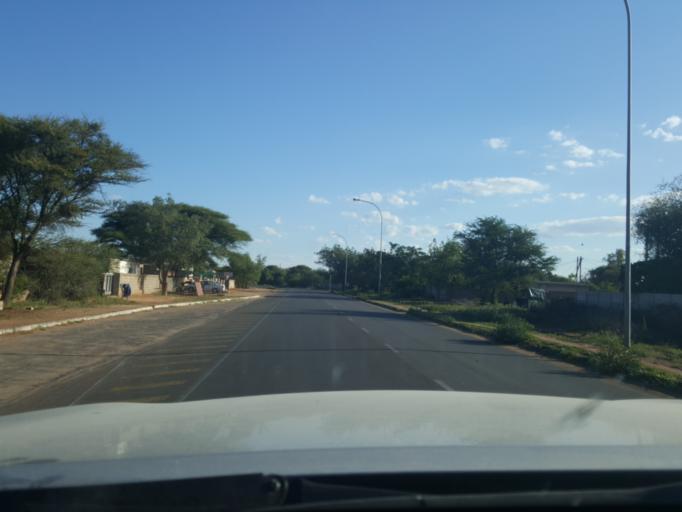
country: BW
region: South East
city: Gaborone
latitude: -24.6197
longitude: 25.9449
